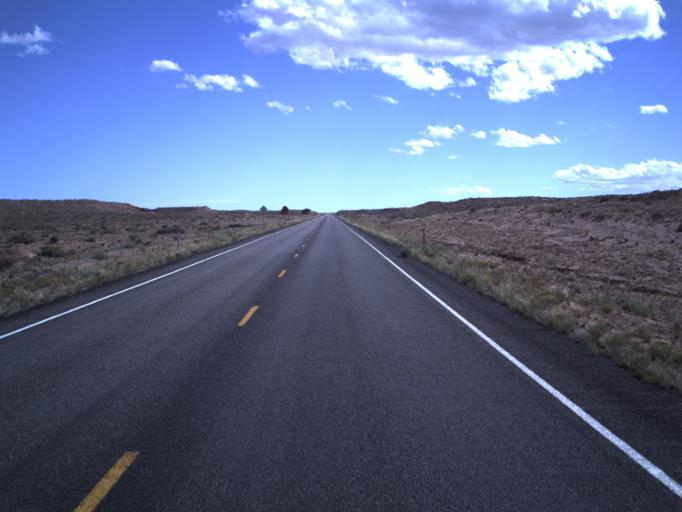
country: US
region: Utah
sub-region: Emery County
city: Ferron
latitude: 38.3645
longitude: -110.7007
